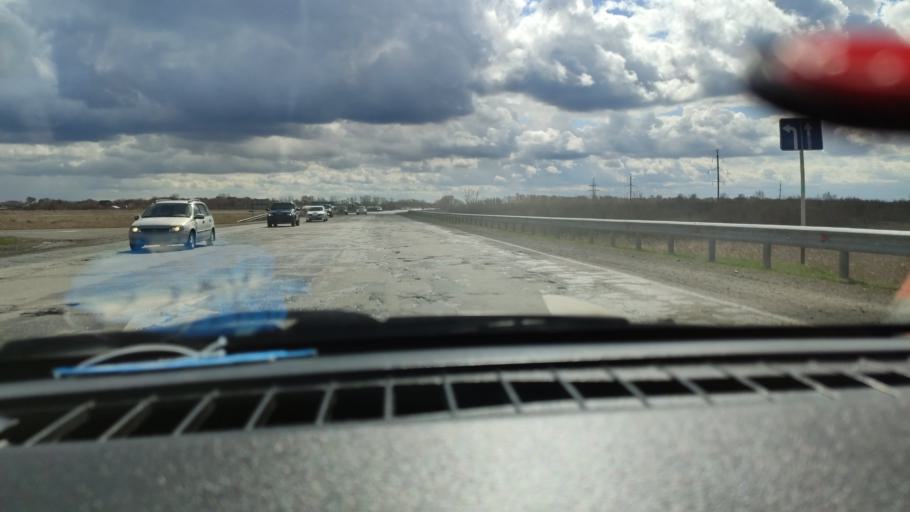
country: RU
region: Samara
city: Tol'yatti
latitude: 53.6650
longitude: 49.4207
